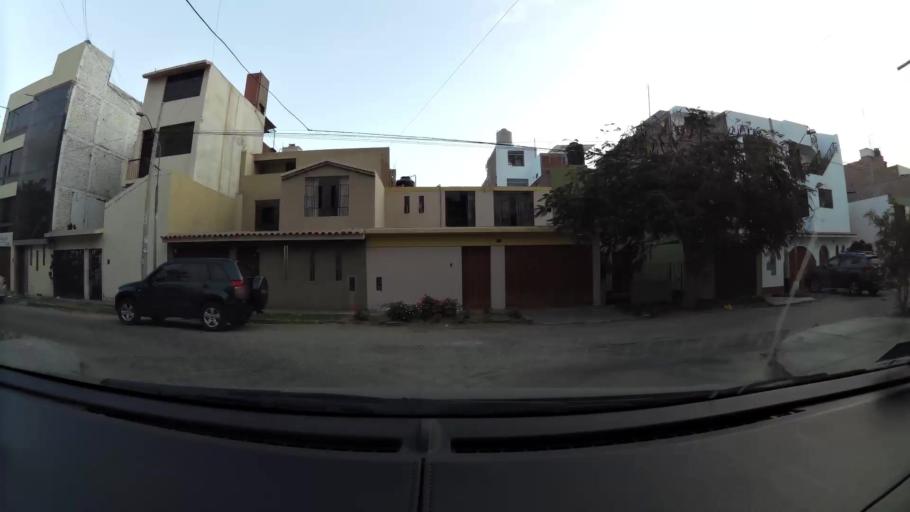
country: PE
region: La Libertad
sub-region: Provincia de Trujillo
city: La Esperanza
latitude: -8.0950
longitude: -79.0340
